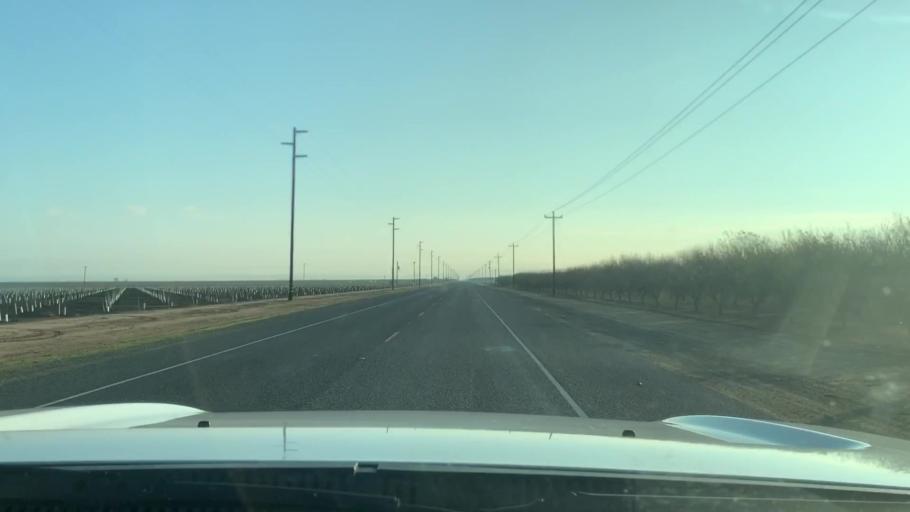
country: US
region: California
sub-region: Kern County
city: Wasco
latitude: 35.6011
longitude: -119.4954
